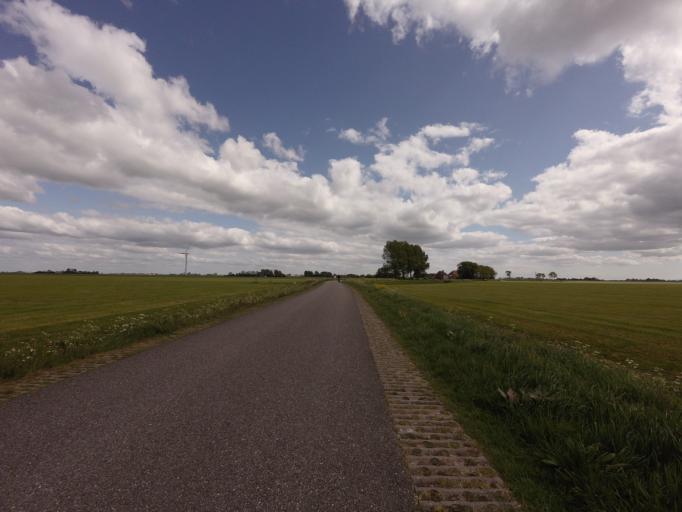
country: NL
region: Friesland
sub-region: Sudwest Fryslan
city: Bolsward
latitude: 53.0821
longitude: 5.5499
